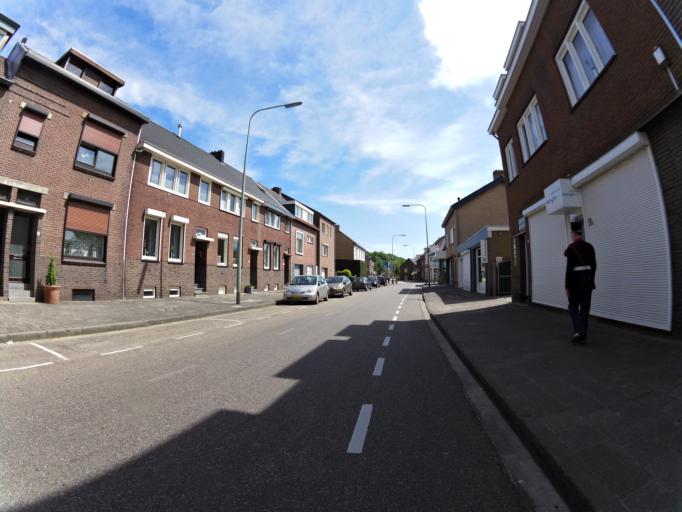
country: NL
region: Limburg
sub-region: Gemeente Simpelveld
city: Simpelveld
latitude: 50.8351
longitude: 5.9775
